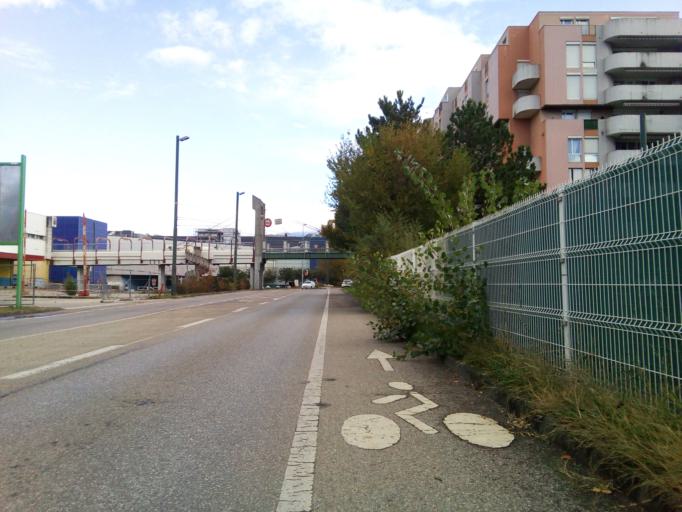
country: FR
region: Rhone-Alpes
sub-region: Departement de l'Isere
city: Echirolles
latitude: 45.1574
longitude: 5.7296
